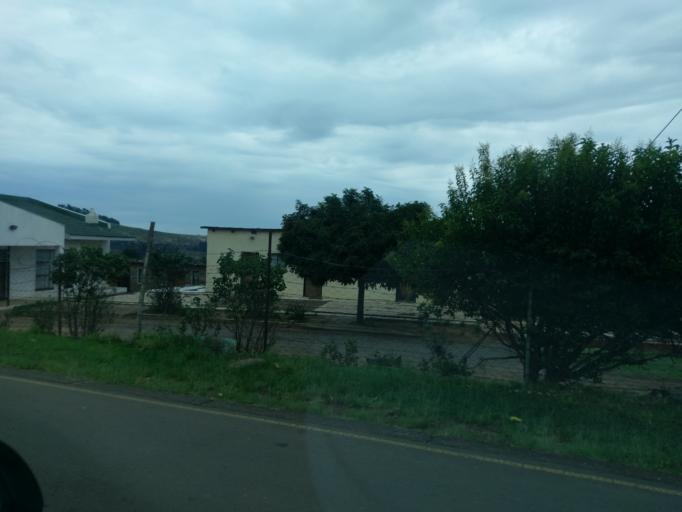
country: LS
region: Berea
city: Teyateyaneng
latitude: -29.1031
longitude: 27.9585
